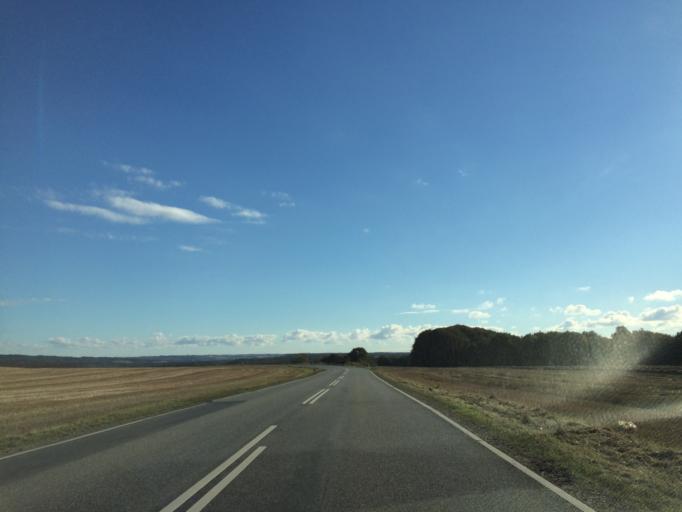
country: DK
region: Central Jutland
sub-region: Randers Kommune
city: Langa
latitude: 56.3454
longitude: 9.8814
